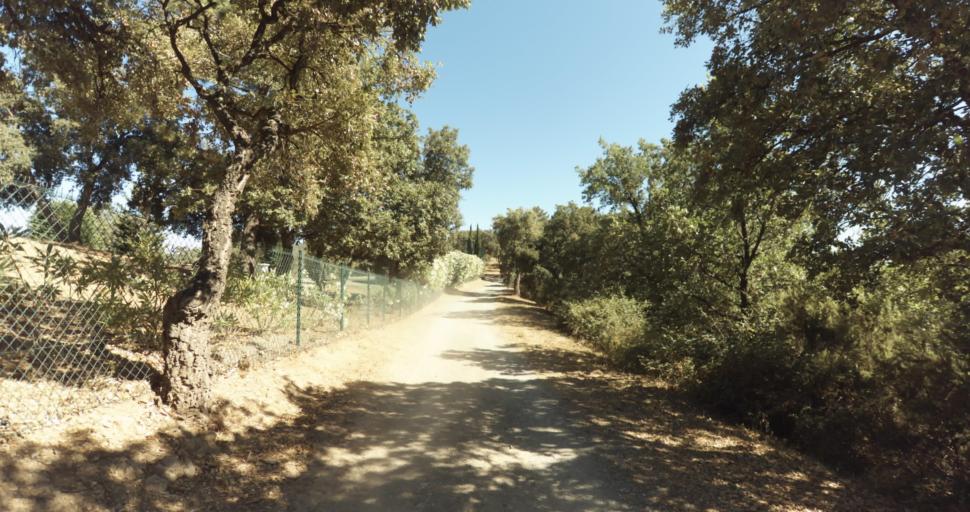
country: FR
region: Provence-Alpes-Cote d'Azur
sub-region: Departement du Var
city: Gassin
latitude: 43.2356
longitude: 6.5849
